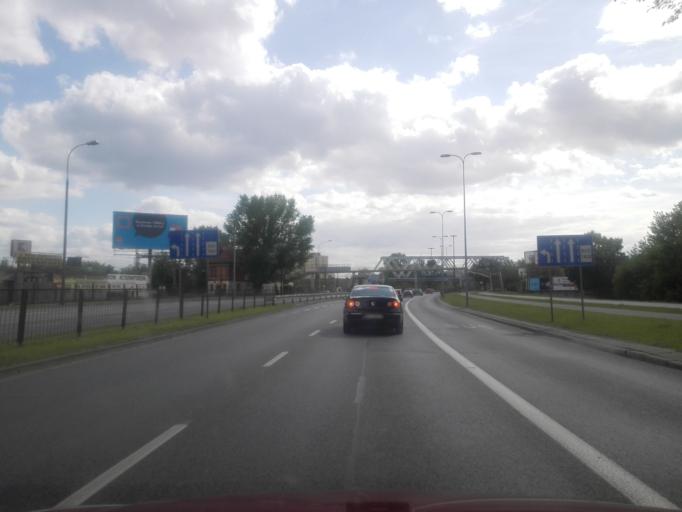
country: PL
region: Masovian Voivodeship
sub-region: Warszawa
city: Praga Polnoc
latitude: 52.2656
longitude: 21.0577
